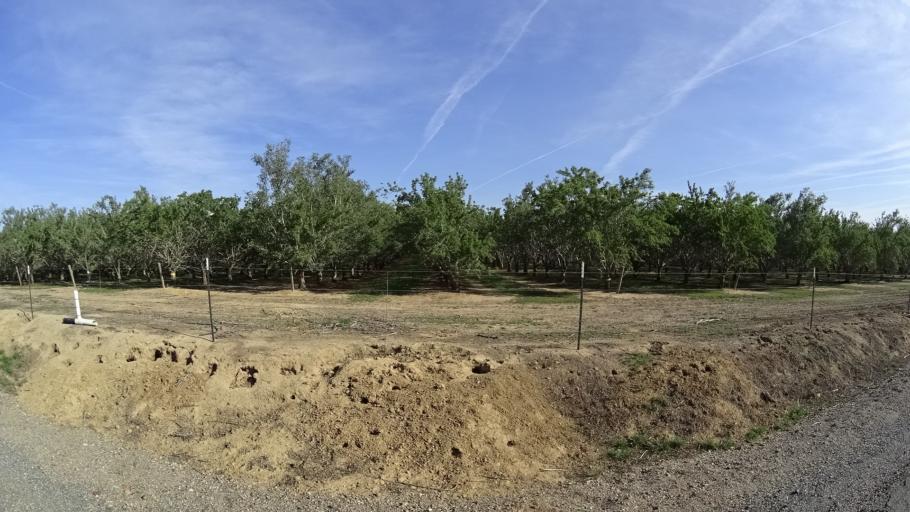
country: US
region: California
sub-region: Glenn County
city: Orland
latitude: 39.6687
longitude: -122.2865
